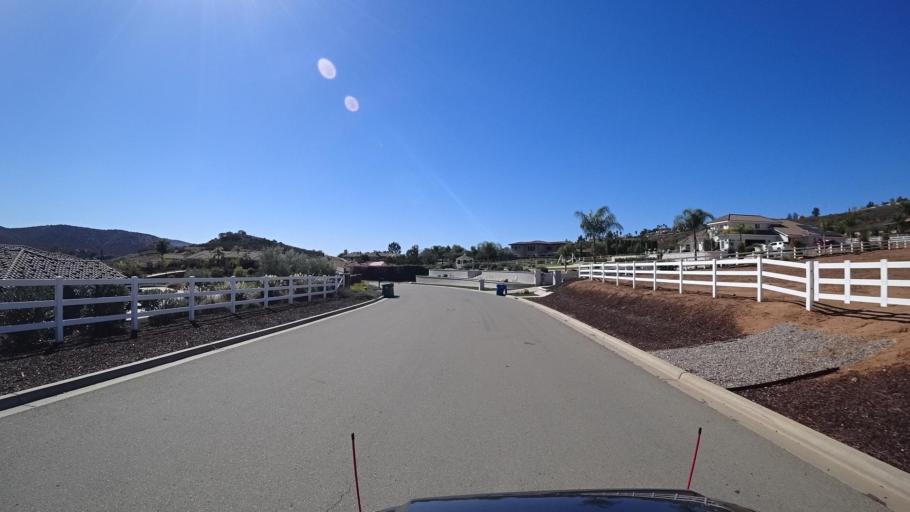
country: US
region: California
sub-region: San Diego County
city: Harbison Canyon
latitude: 32.8589
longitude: -116.8635
